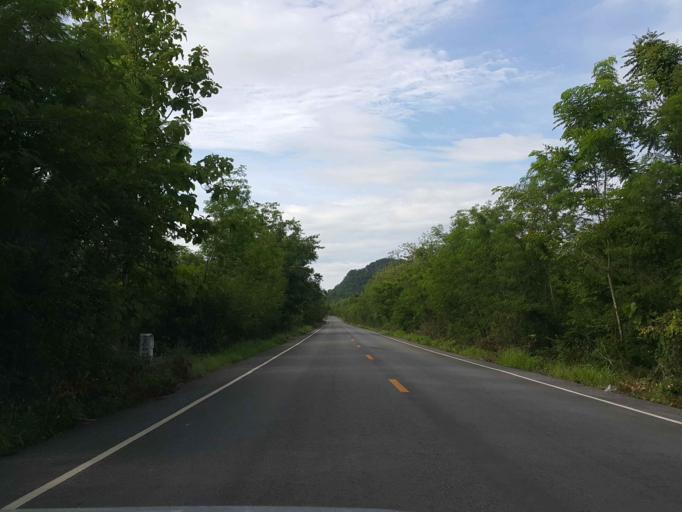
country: TH
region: Sukhothai
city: Thung Saliam
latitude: 17.2943
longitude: 99.5269
